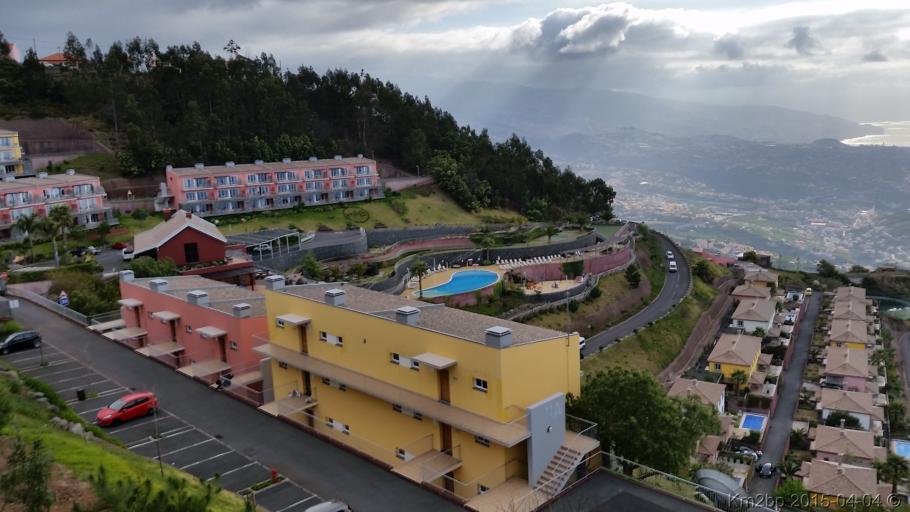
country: PT
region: Madeira
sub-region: Ribeira Brava
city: Campanario
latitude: 32.6573
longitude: -17.0045
